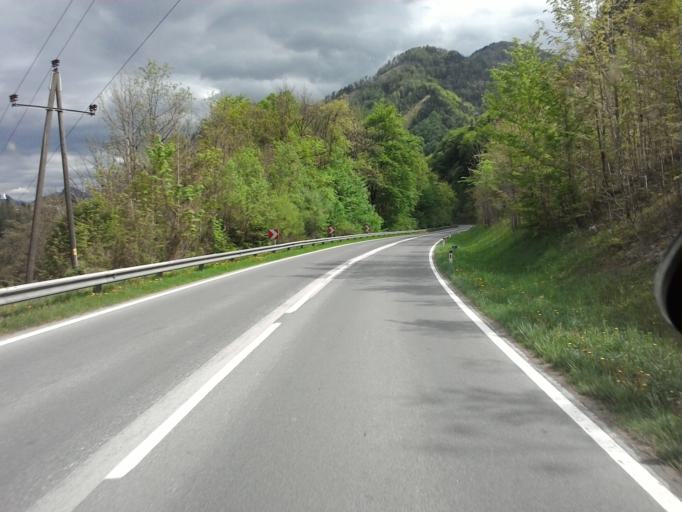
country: AT
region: Upper Austria
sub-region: Politischer Bezirk Kirchdorf an der Krems
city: Micheldorf in Oberoesterreich
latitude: 47.7766
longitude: 14.1658
